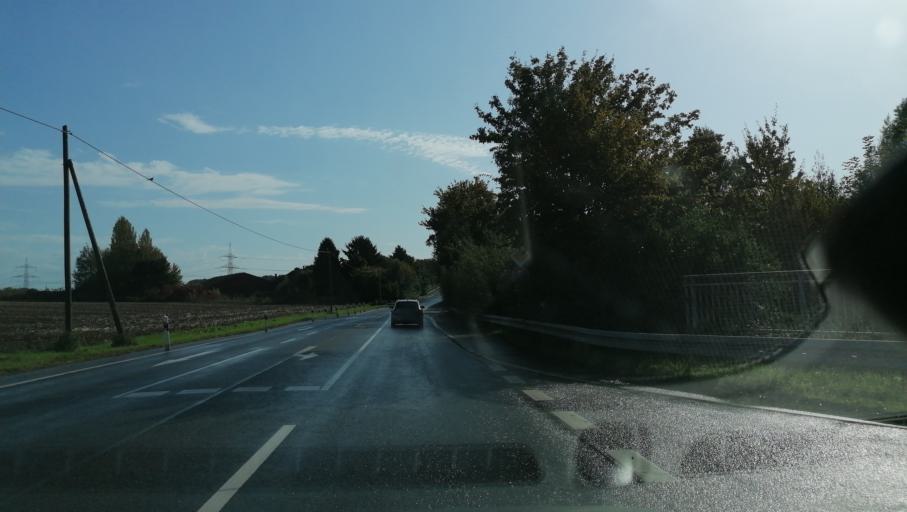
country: DE
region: North Rhine-Westphalia
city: Datteln
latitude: 51.6362
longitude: 7.3475
